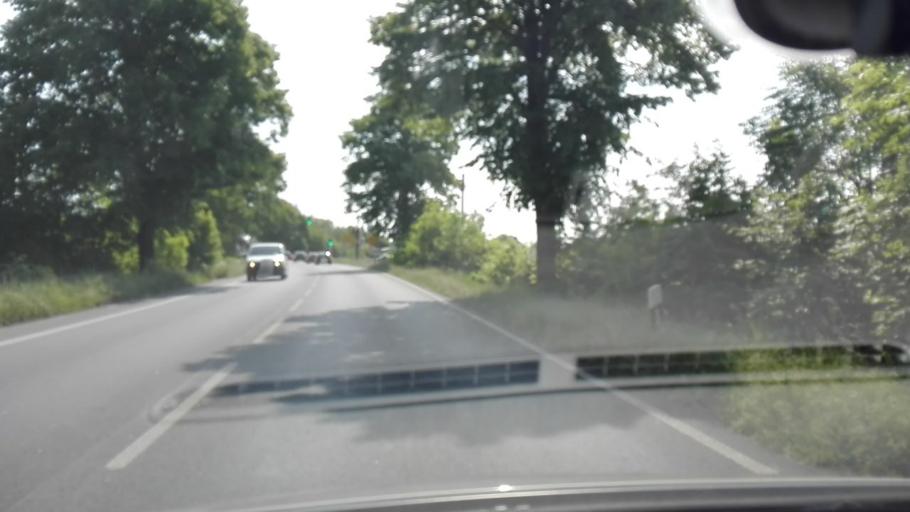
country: DE
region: North Rhine-Westphalia
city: Bergkamen
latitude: 51.5895
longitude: 7.6278
